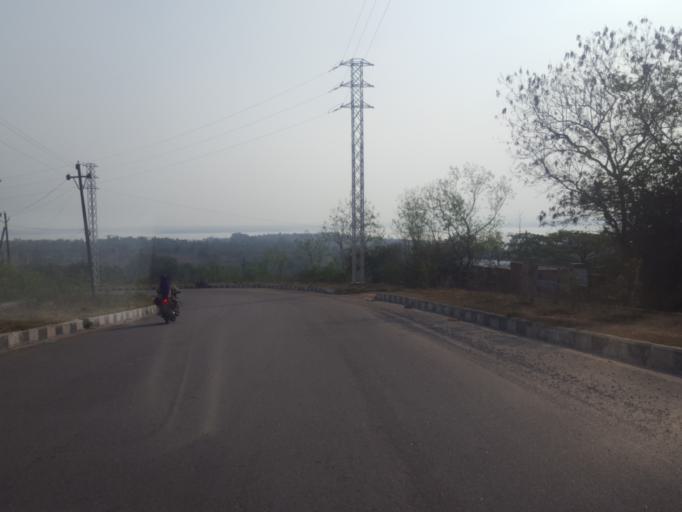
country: IN
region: Telangana
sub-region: Medak
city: Serilingampalle
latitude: 17.4010
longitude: 78.3107
